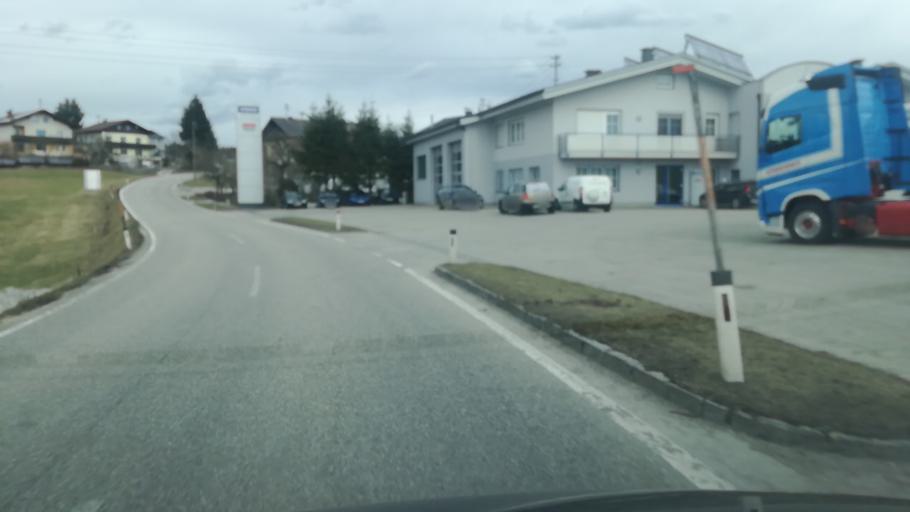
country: AT
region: Upper Austria
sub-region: Politischer Bezirk Vocklabruck
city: Frankenburg
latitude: 48.0854
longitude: 13.4832
